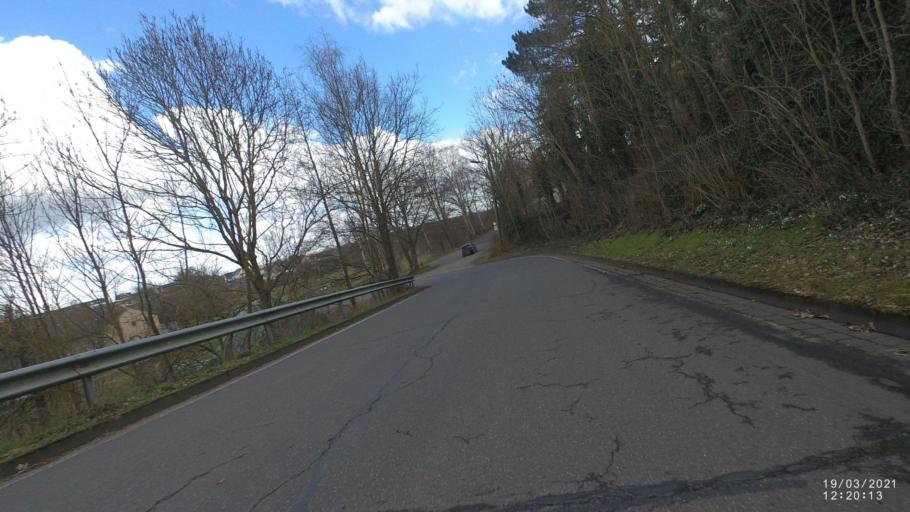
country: DE
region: Rheinland-Pfalz
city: Kretz
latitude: 50.3923
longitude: 7.3615
